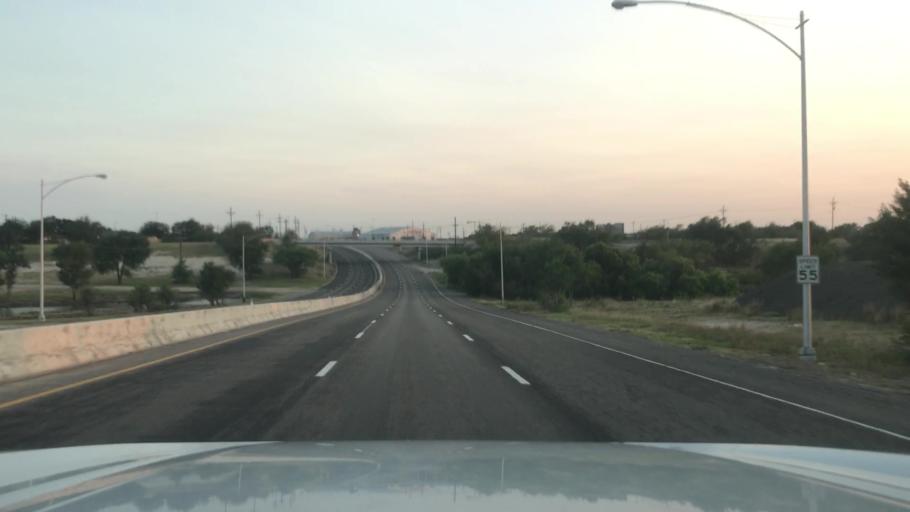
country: US
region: Texas
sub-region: Lubbock County
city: Lubbock
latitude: 33.6047
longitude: -101.8520
